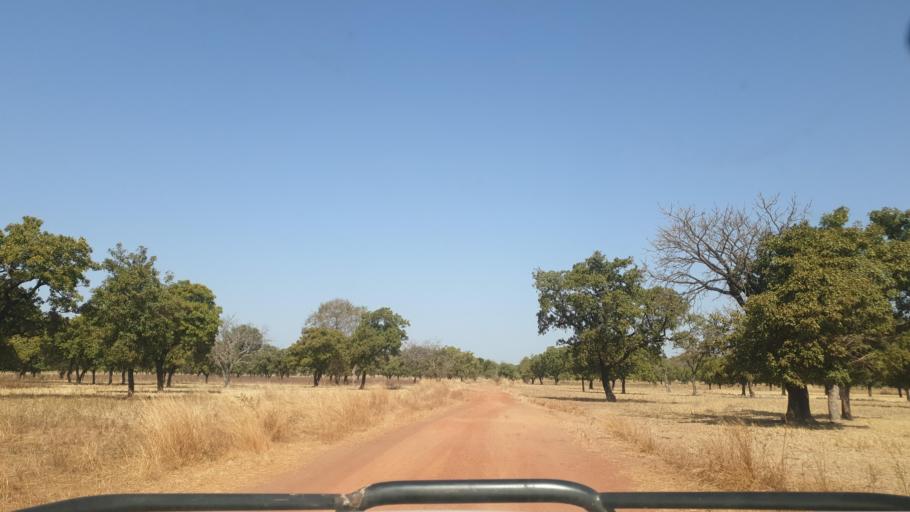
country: ML
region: Koulikoro
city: Dioila
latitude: 11.9003
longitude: -6.9816
